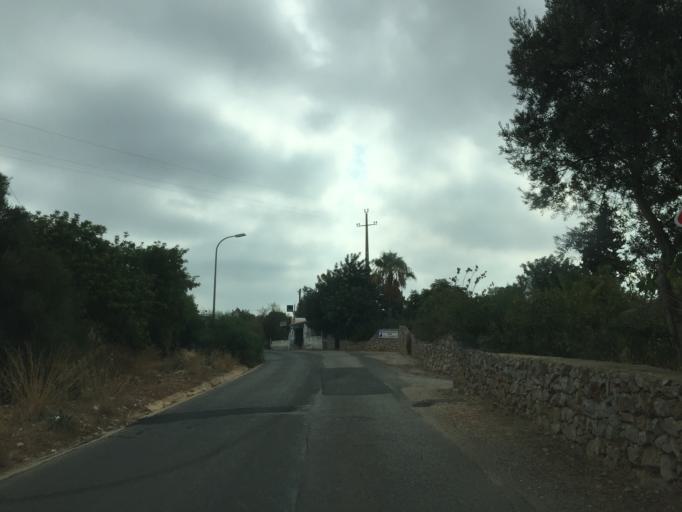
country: PT
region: Faro
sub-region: Faro
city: Santa Barbara de Nexe
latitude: 37.1005
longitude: -7.9671
